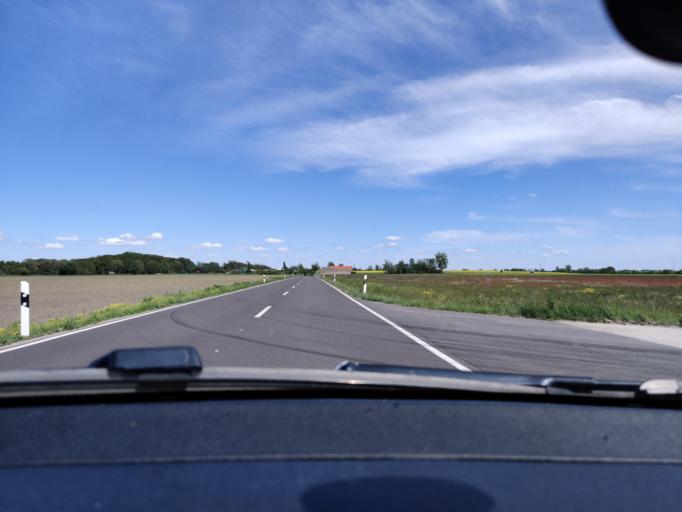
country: DE
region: Saxony-Anhalt
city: Mockern
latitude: 52.1130
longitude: 11.9059
